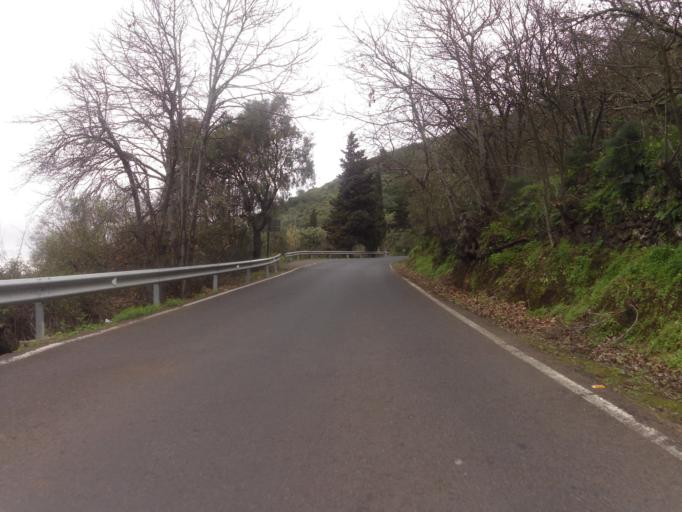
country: ES
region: Canary Islands
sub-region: Provincia de Las Palmas
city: Vega de San Mateo
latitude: 27.9990
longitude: -15.5404
